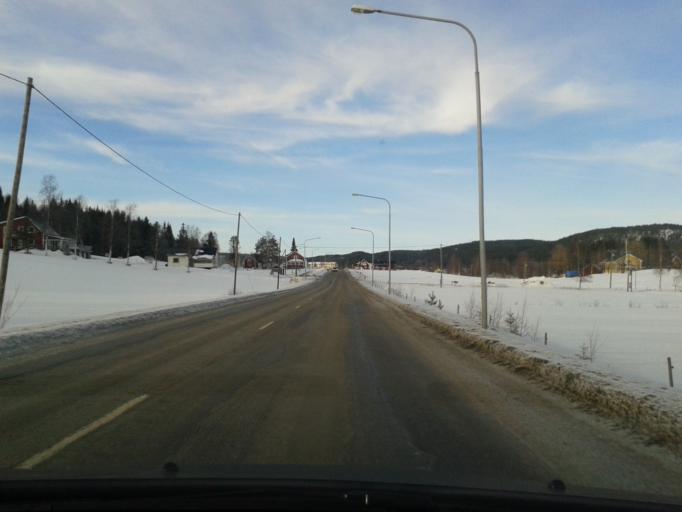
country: SE
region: Vaesternorrland
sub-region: OErnskoeldsviks Kommun
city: Bredbyn
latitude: 63.5079
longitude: 18.0697
